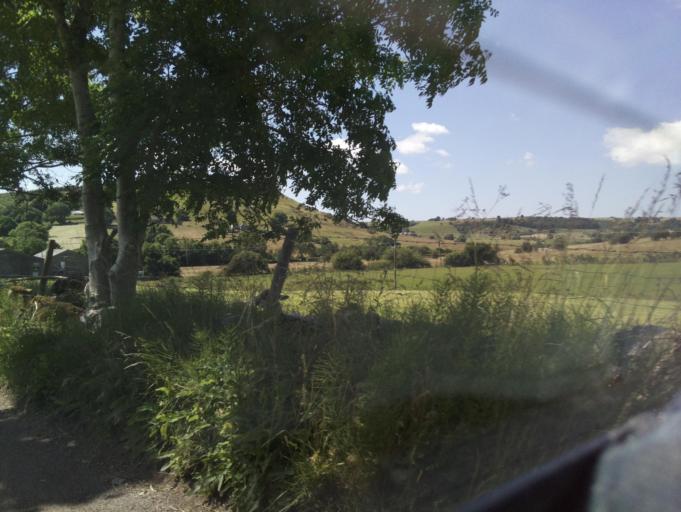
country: GB
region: England
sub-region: Derbyshire
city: Buxton
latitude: 53.1981
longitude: -1.8753
